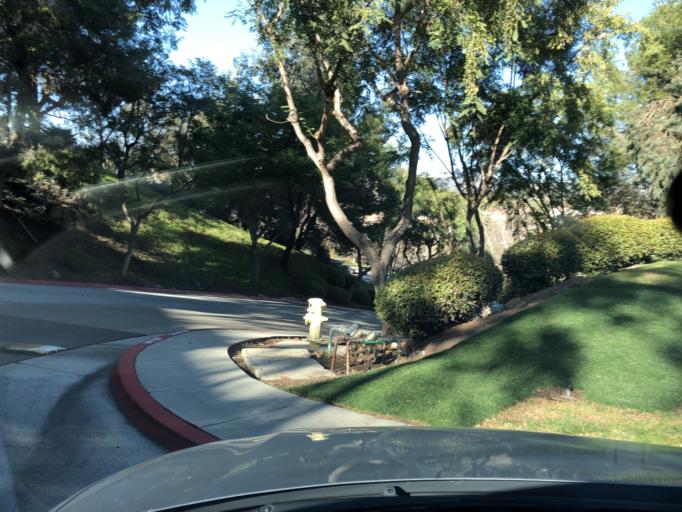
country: US
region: California
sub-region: San Diego County
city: Escondido
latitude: 33.1364
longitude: -117.0959
